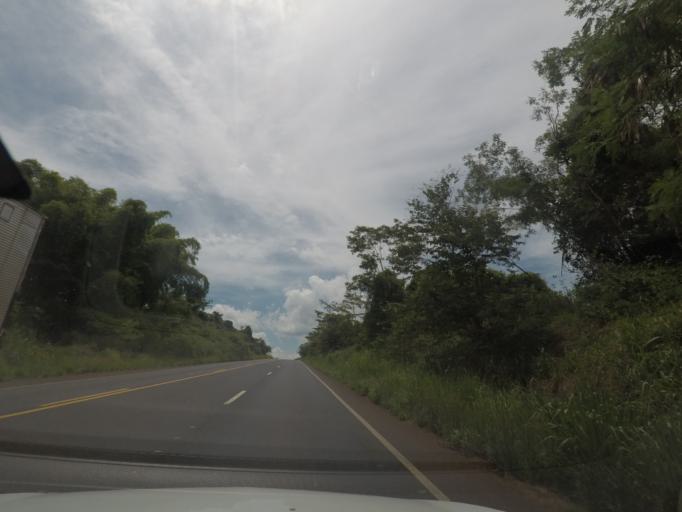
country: BR
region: Sao Paulo
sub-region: Barretos
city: Barretos
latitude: -20.4225
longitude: -48.6301
